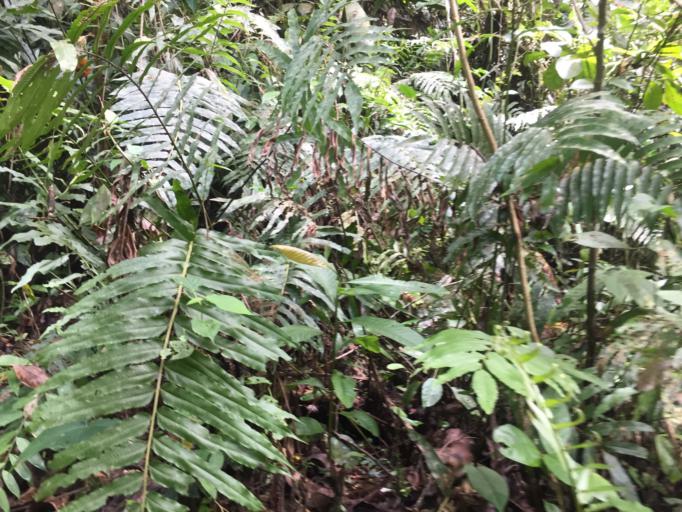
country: PE
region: Cusco
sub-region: Provincia de Paucartambo
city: Pillcopata
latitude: -12.8112
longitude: -71.3964
